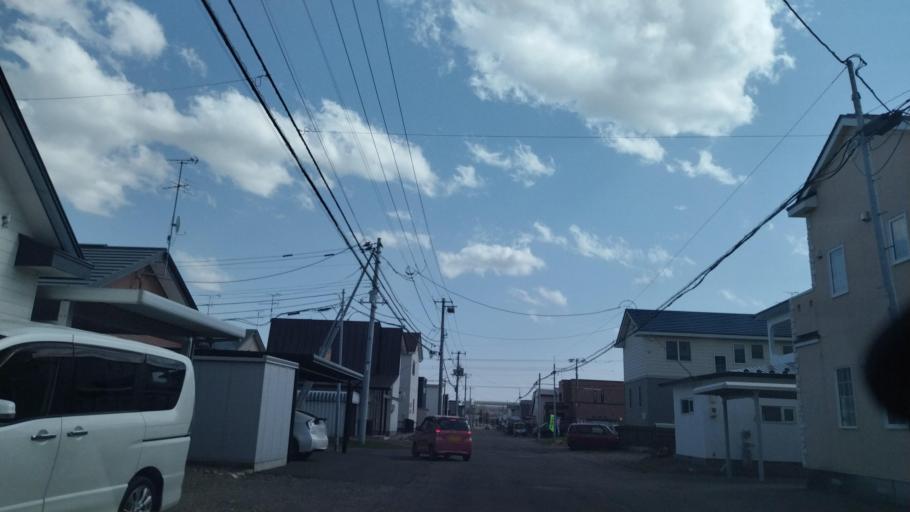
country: JP
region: Hokkaido
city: Obihiro
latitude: 42.9375
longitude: 143.1655
